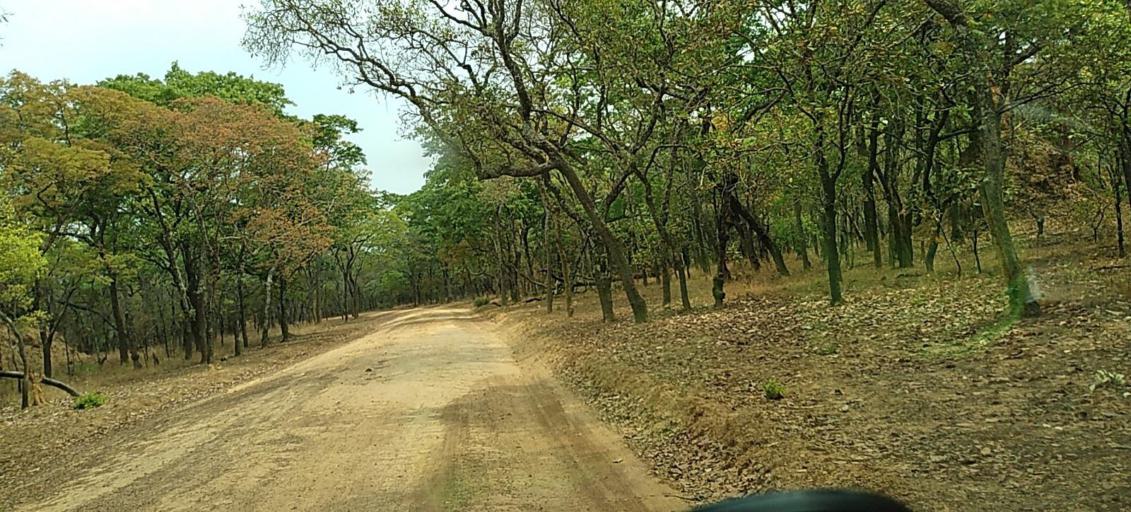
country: ZM
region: North-Western
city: Solwezi
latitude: -12.9402
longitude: 26.5581
